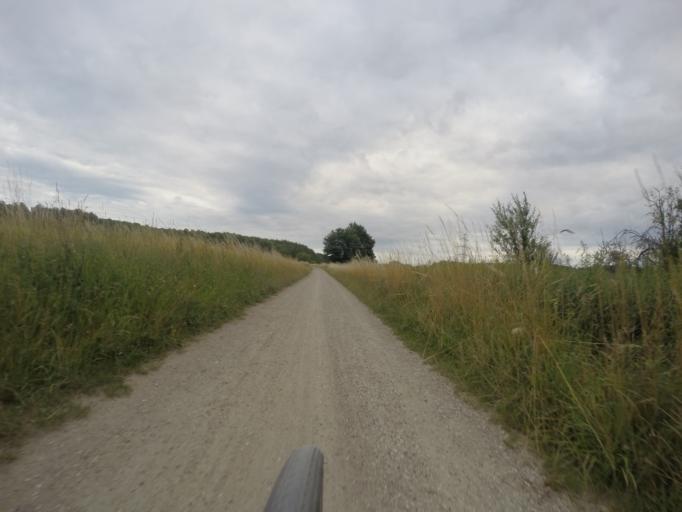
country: DK
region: Capital Region
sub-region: Hoje-Taastrup Kommune
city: Taastrup
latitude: 55.6915
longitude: 12.3182
